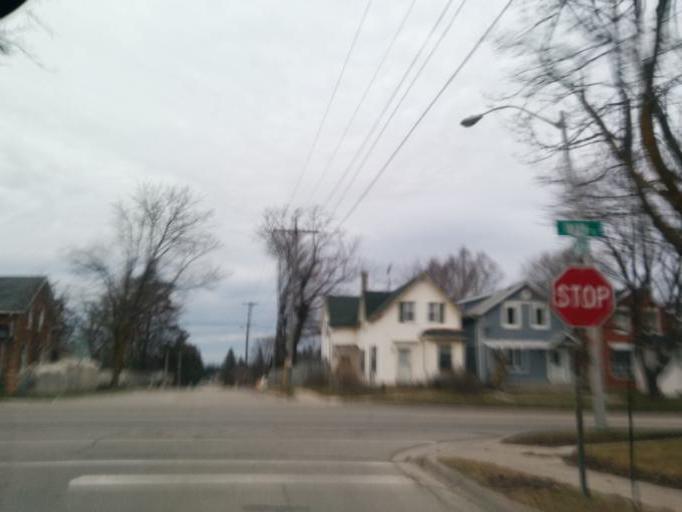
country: CA
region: Ontario
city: Shelburne
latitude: 44.0793
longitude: -80.1990
